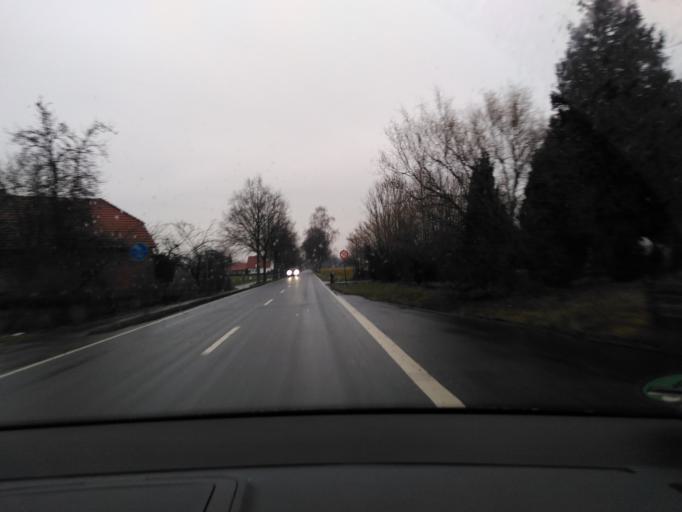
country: DE
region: North Rhine-Westphalia
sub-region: Regierungsbezirk Detmold
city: Verl
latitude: 51.8904
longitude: 8.4832
